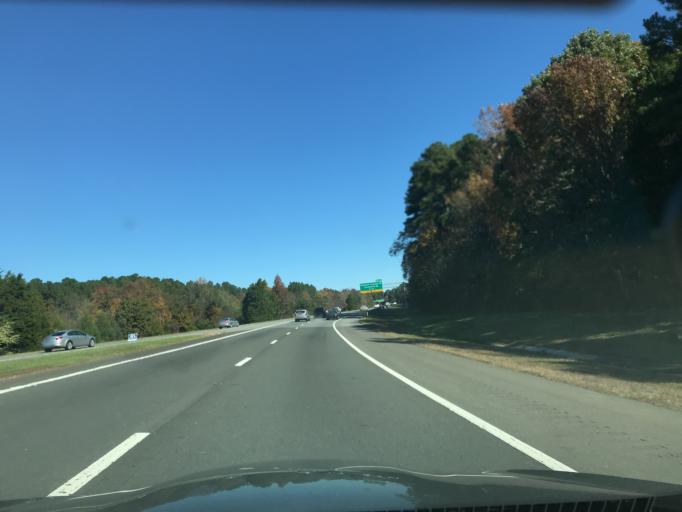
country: US
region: North Carolina
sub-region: Wake County
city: Morrisville
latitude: 35.9048
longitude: -78.8704
